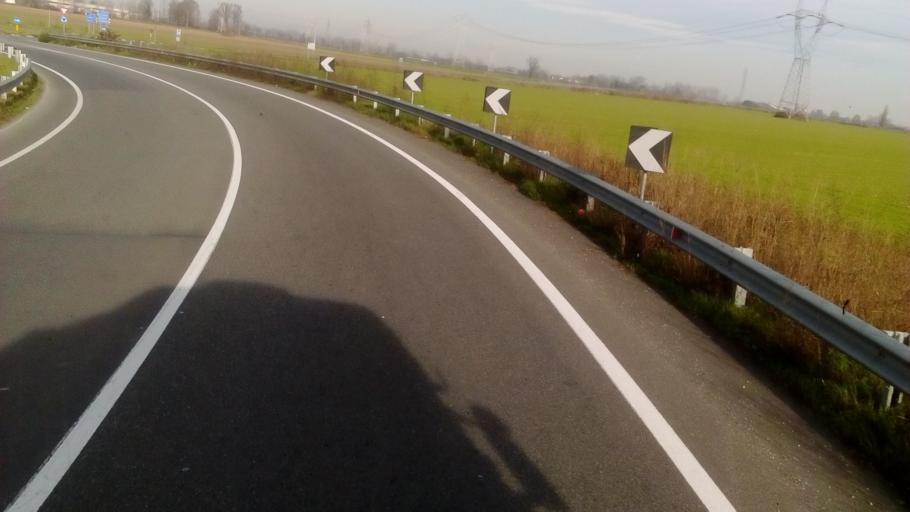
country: IT
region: Lombardy
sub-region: Provincia di Lodi
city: Casalpusterlengo
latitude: 45.1637
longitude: 9.6624
